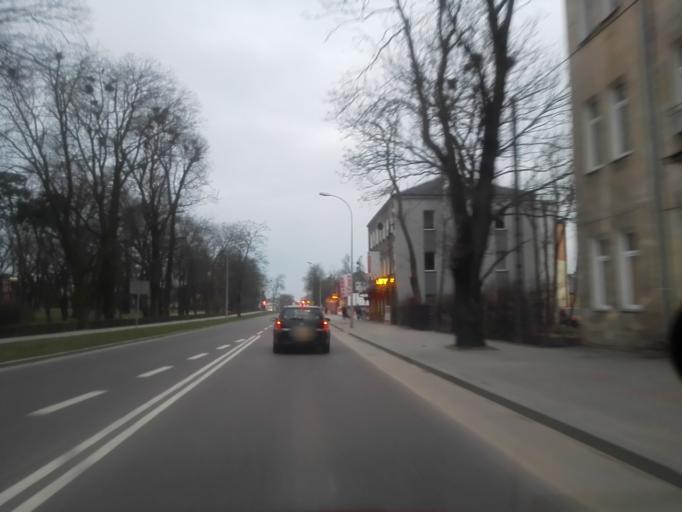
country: PL
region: Podlasie
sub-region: Lomza
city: Lomza
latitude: 53.1763
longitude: 22.0714
